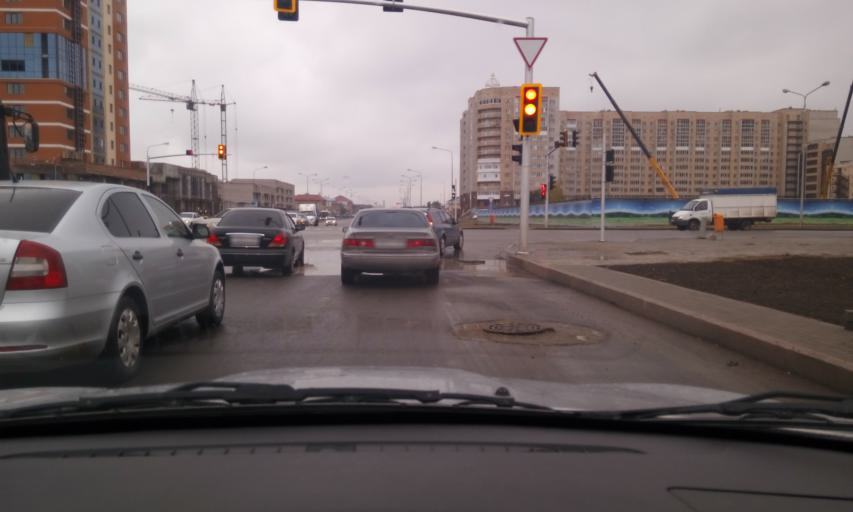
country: KZ
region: Astana Qalasy
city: Astana
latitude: 51.1287
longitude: 71.4977
